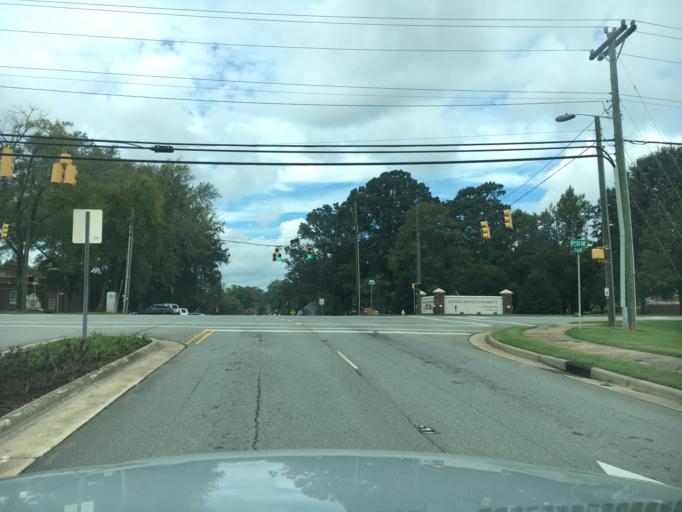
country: US
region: North Carolina
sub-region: Catawba County
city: Hickory
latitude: 35.7371
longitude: -81.3251
